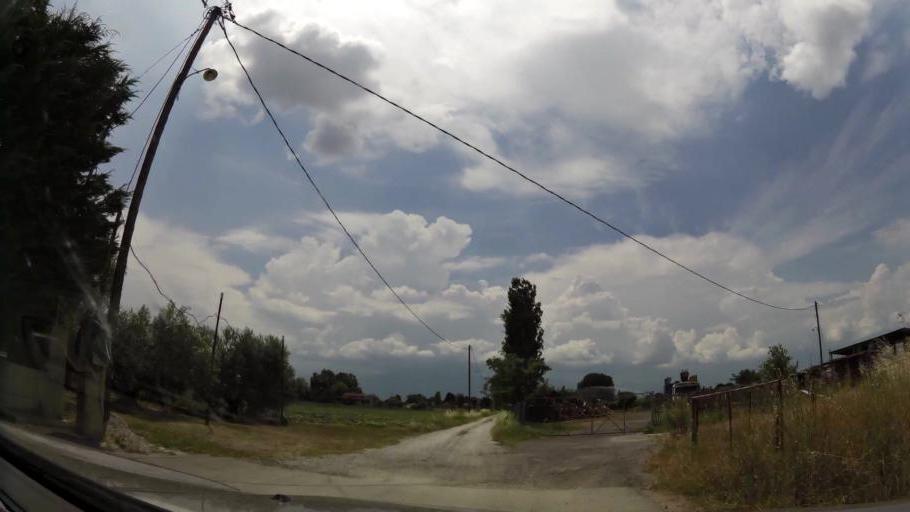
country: GR
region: Central Macedonia
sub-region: Nomos Pierias
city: Peristasi
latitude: 40.2706
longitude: 22.5475
